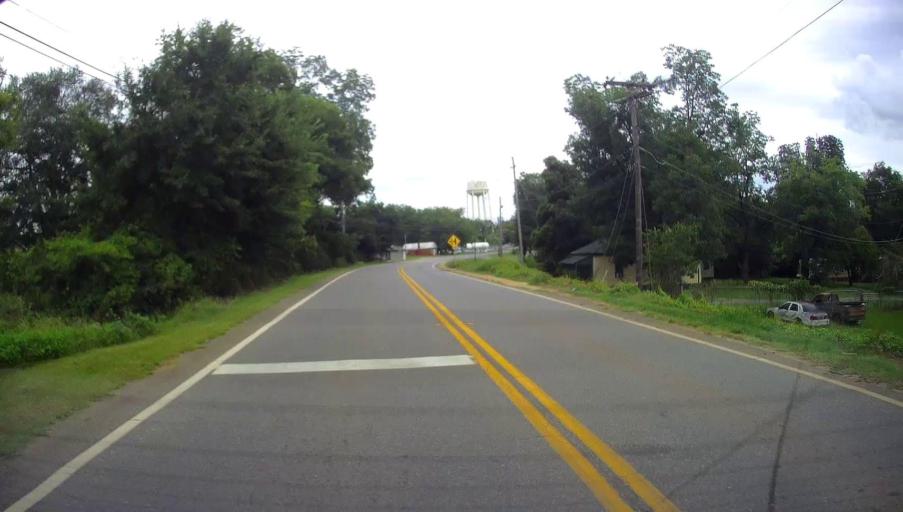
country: US
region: Georgia
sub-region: Marion County
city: Buena Vista
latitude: 32.3183
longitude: -84.5113
